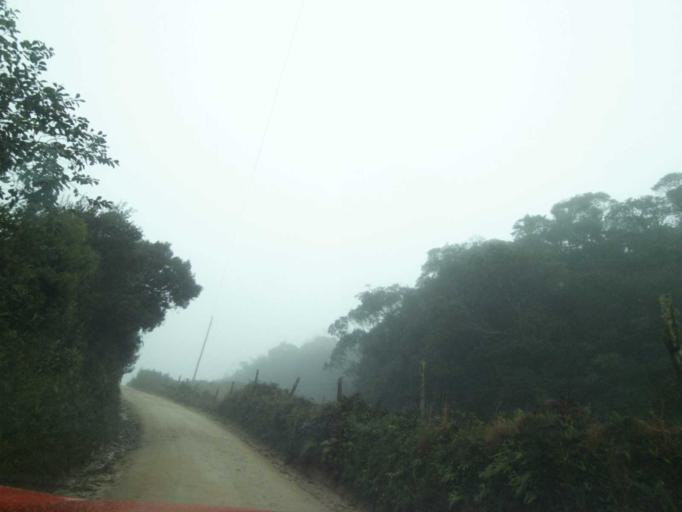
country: BR
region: Santa Catarina
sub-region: Anitapolis
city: Anitapolis
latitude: -27.9098
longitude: -49.1692
